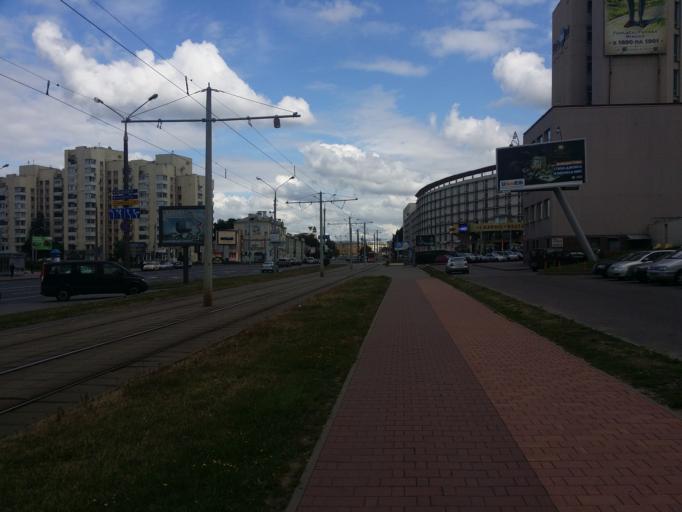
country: BY
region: Minsk
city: Minsk
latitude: 53.9168
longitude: 27.5617
